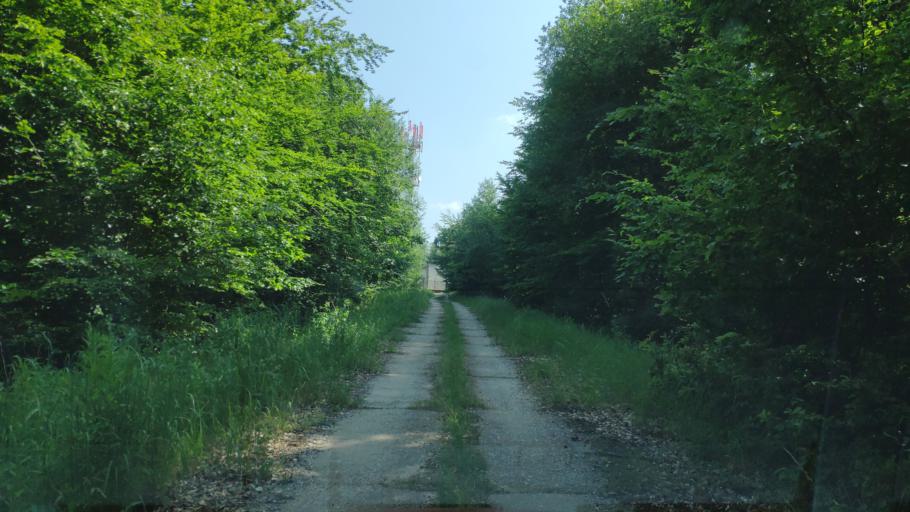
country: SK
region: Presovsky
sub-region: Okres Presov
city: Presov
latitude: 48.9716
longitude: 21.1499
